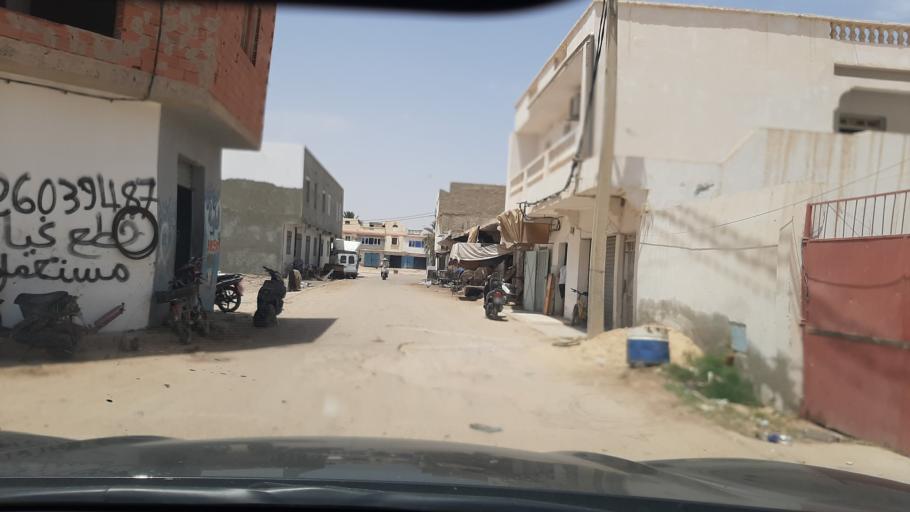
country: TN
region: Qabis
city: Gabes
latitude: 33.6192
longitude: 10.2905
